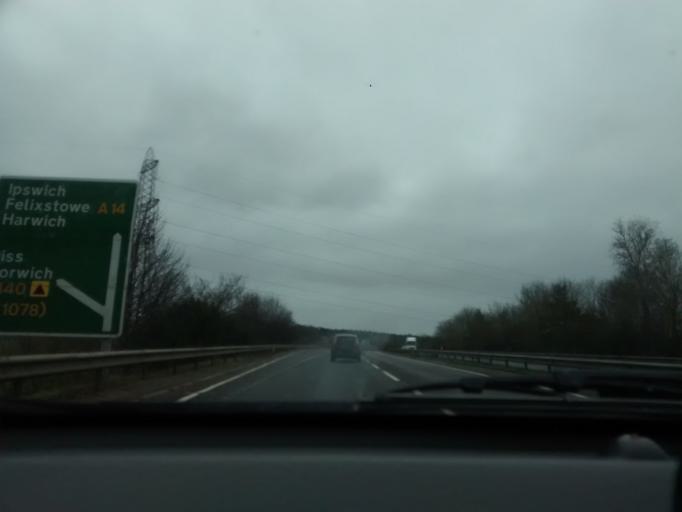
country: GB
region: England
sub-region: Suffolk
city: Needham Market
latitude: 52.1502
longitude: 1.0743
